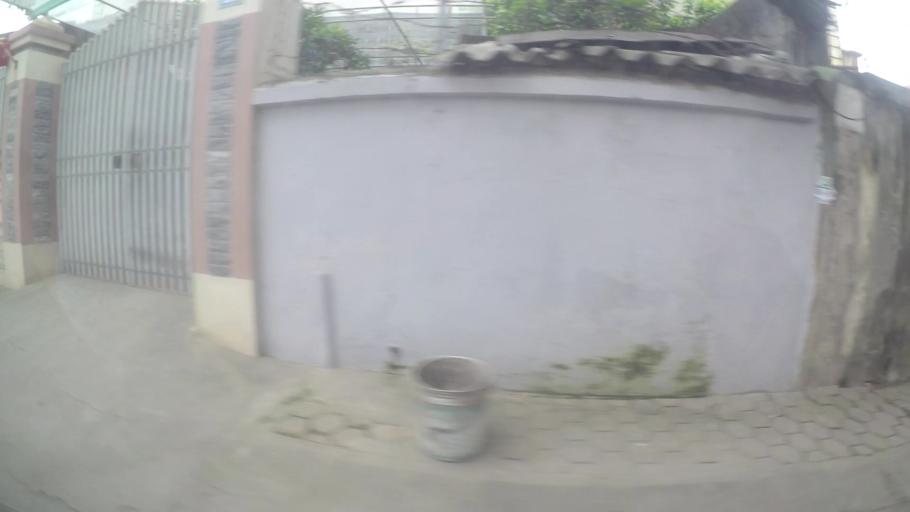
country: VN
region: Ha Noi
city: Cau Dien
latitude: 21.0358
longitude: 105.7408
